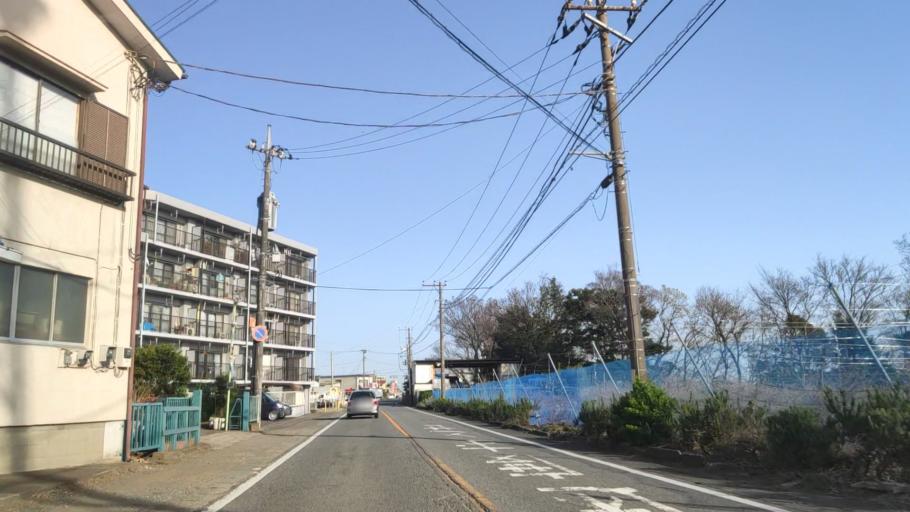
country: JP
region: Kanagawa
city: Zama
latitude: 35.5056
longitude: 139.3473
